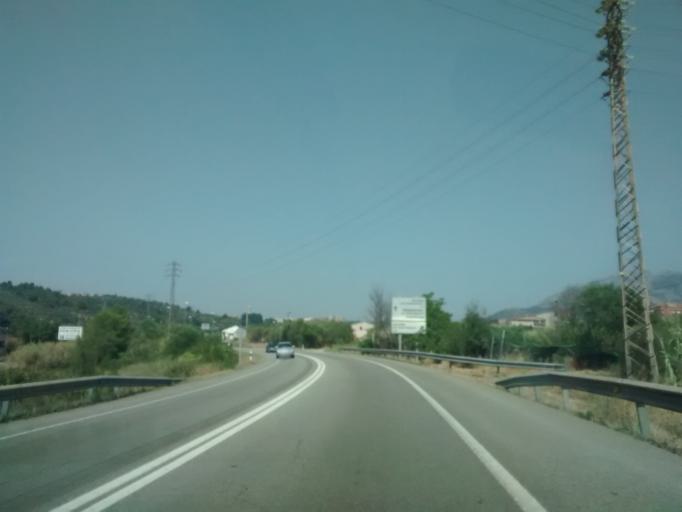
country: ES
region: Catalonia
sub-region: Provincia de Barcelona
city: Olesa de Montserrat
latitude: 41.5366
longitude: 1.8973
